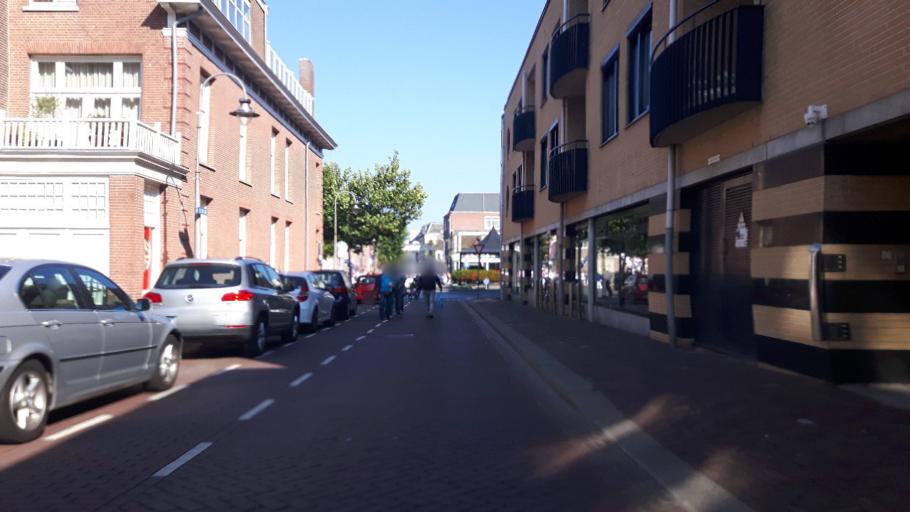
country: NL
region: North Holland
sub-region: Gemeente Zandvoort
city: Zandvoort
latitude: 52.3714
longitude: 4.5301
